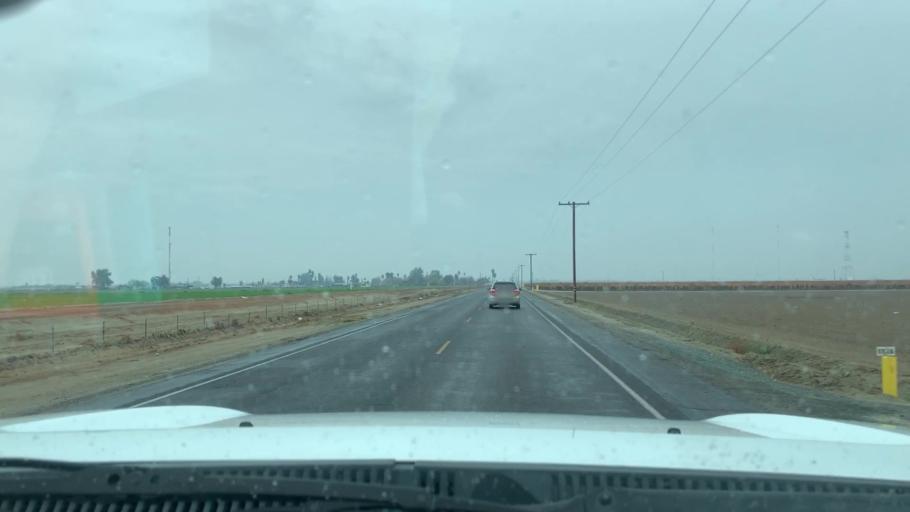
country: US
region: California
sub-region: Kern County
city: Delano
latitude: 35.7613
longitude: -119.3008
